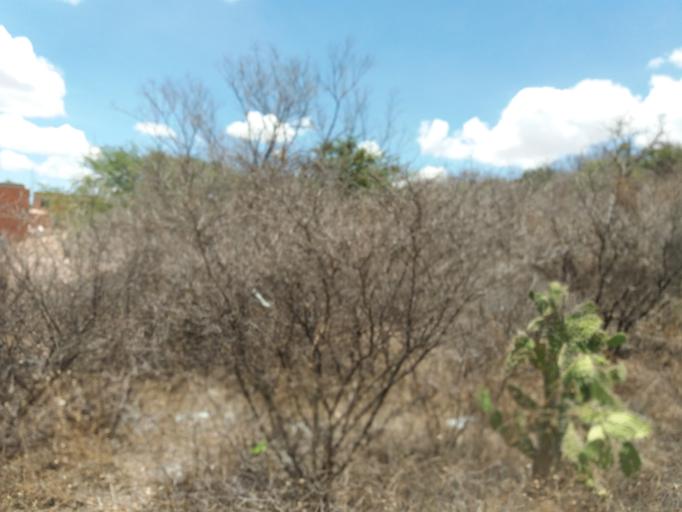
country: MX
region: Aguascalientes
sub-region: Aguascalientes
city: San Sebastian [Fraccionamiento]
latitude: 21.7837
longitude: -102.2524
